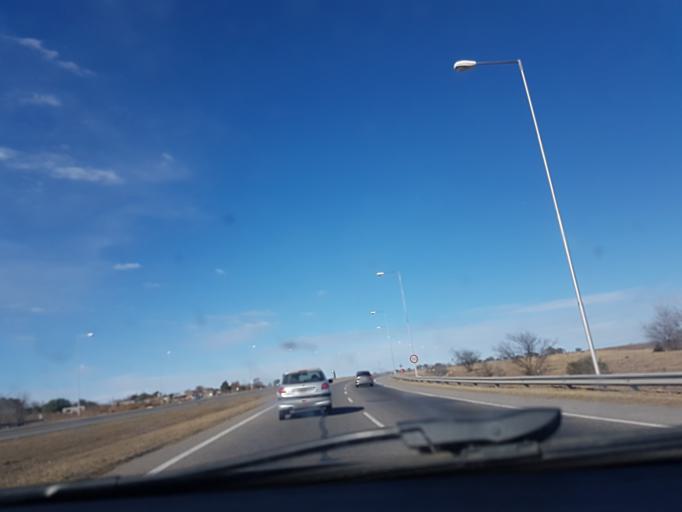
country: AR
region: Cordoba
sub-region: Departamento de Capital
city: Cordoba
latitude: -31.4162
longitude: -64.2696
